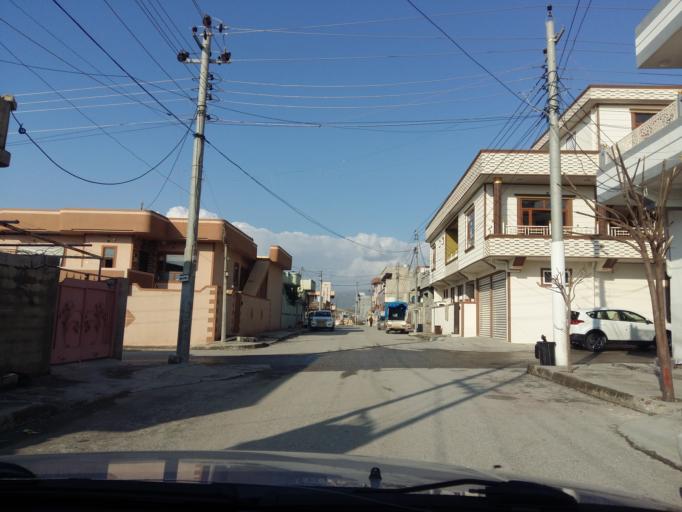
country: IQ
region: As Sulaymaniyah
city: Qeladize
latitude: 36.1766
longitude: 45.1381
